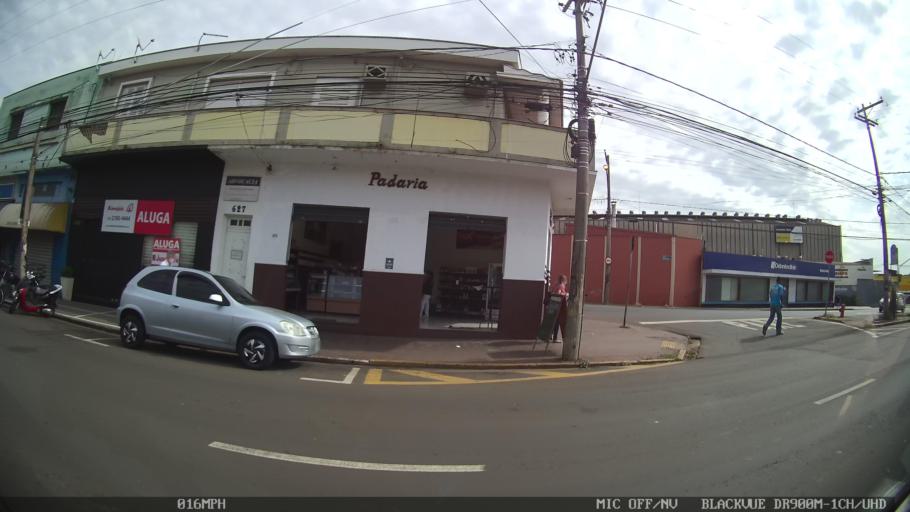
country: BR
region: Sao Paulo
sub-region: Piracicaba
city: Piracicaba
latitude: -22.7084
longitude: -47.6538
